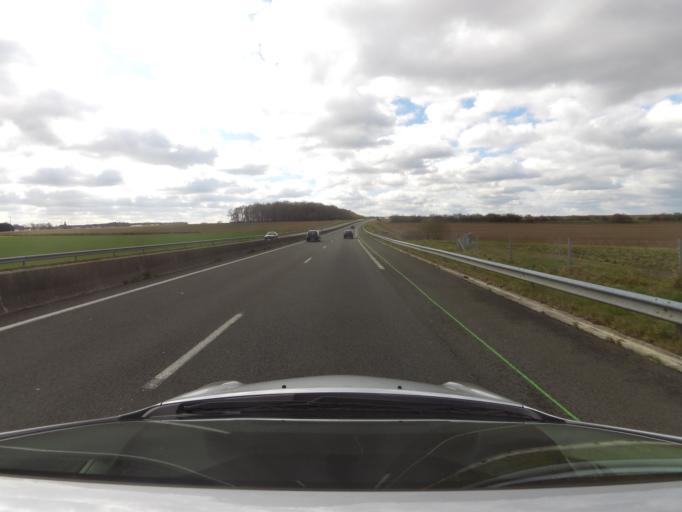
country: FR
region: Picardie
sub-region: Departement de la Somme
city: Sailly-Flibeaucourt
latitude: 50.1933
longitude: 1.7583
